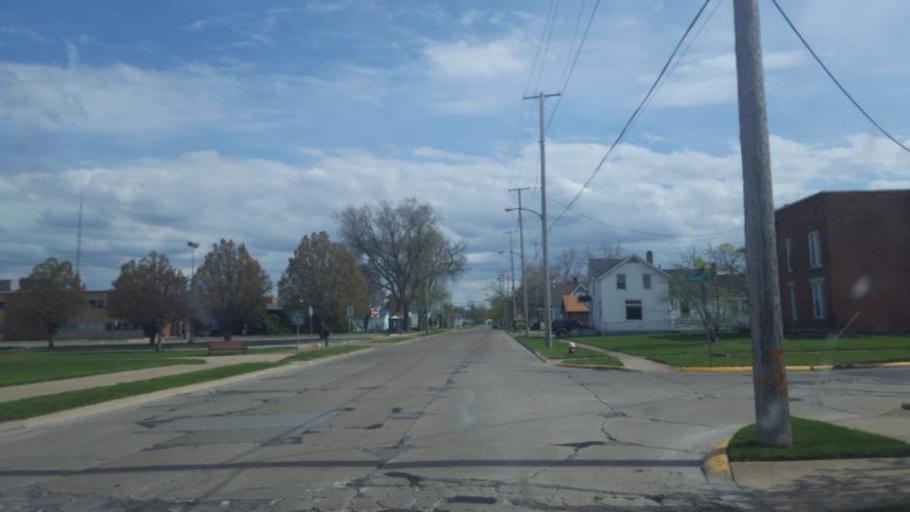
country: US
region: Ohio
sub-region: Erie County
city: Sandusky
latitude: 41.4595
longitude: -82.7024
